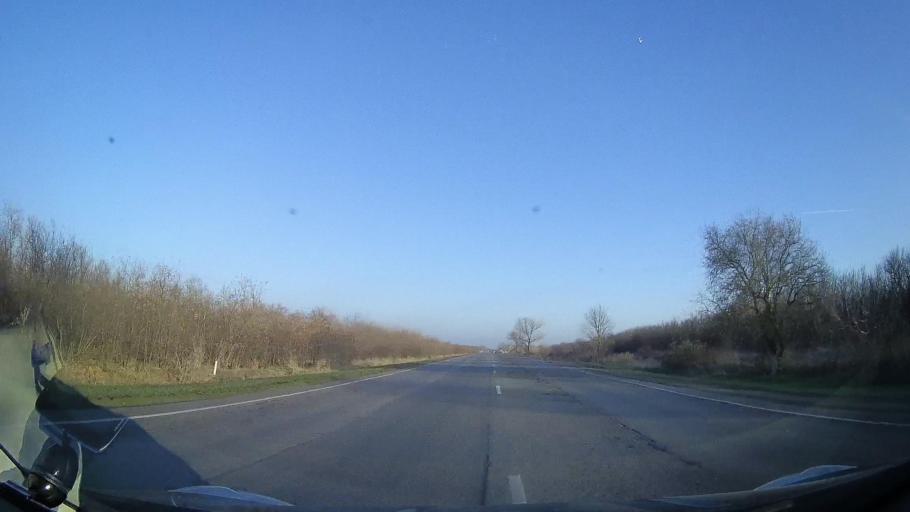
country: RU
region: Rostov
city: Kirovskaya
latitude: 47.0156
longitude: 39.9133
